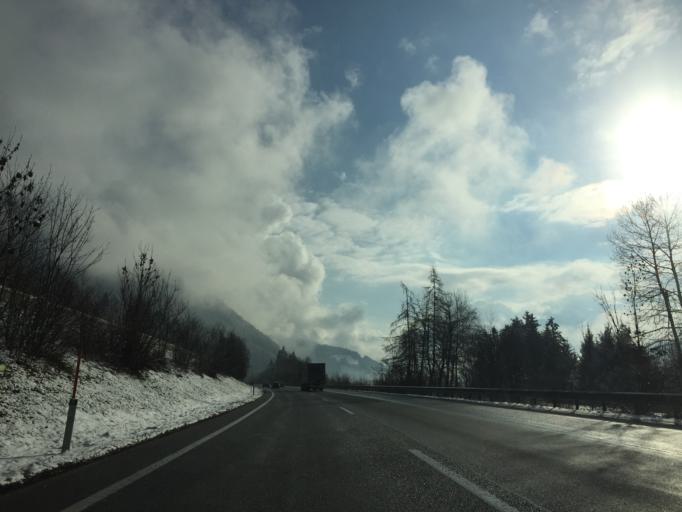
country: AT
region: Salzburg
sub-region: Politischer Bezirk Sankt Johann im Pongau
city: Werfenweng
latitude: 47.4343
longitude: 13.2550
